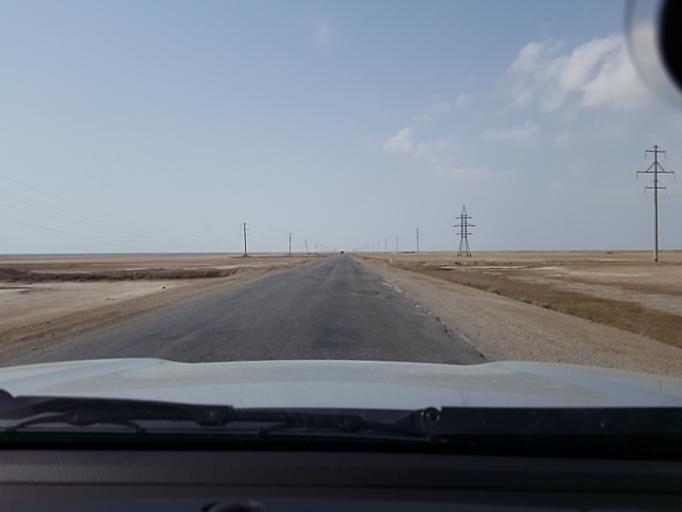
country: TM
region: Balkan
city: Gumdag
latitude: 39.0836
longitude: 54.5844
